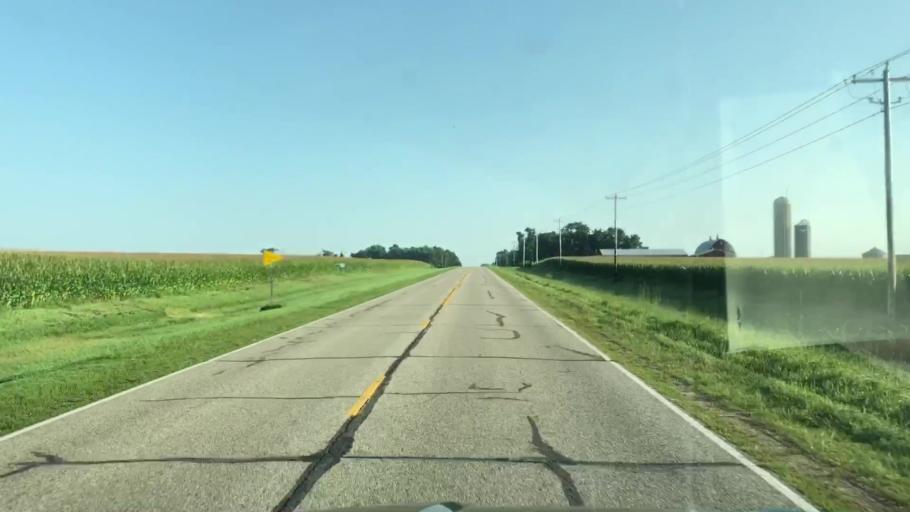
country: US
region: Iowa
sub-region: Lyon County
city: George
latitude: 43.3698
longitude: -95.9983
